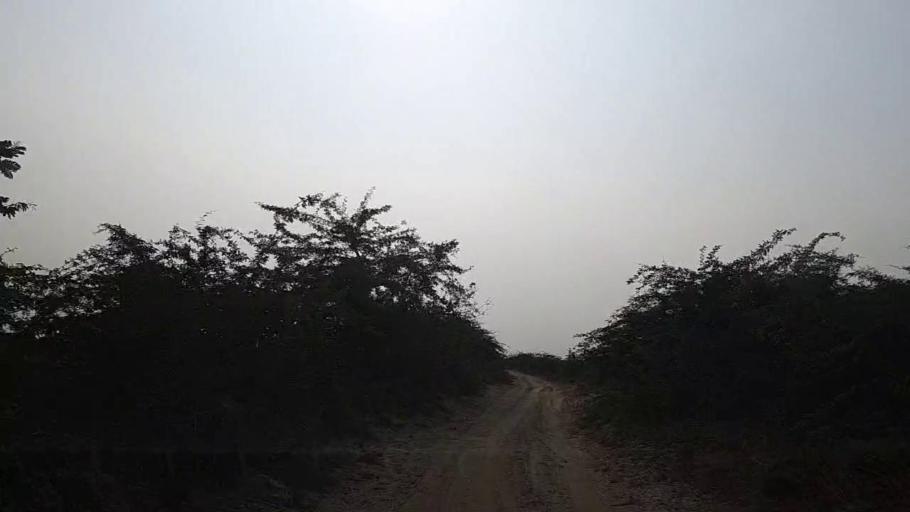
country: PK
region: Sindh
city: Gharo
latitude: 24.6593
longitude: 67.6249
